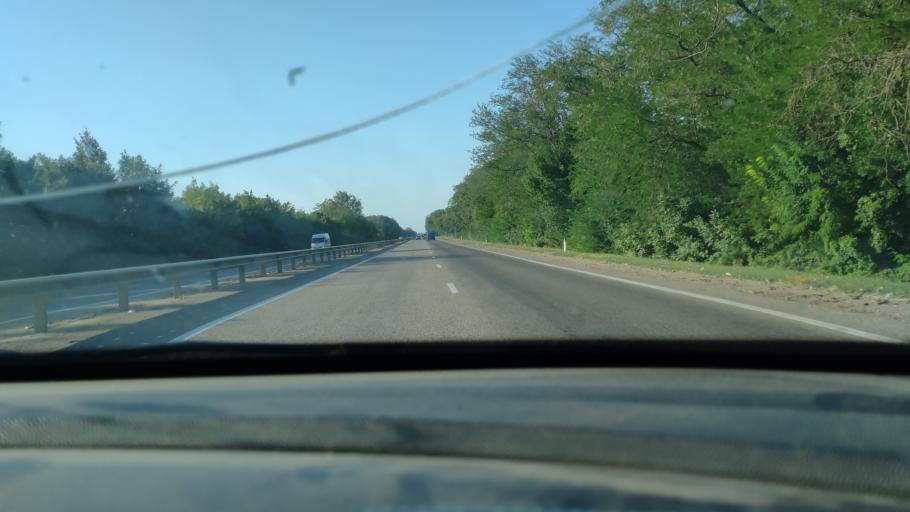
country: RU
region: Krasnodarskiy
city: Timashevsk
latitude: 45.5340
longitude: 38.9387
